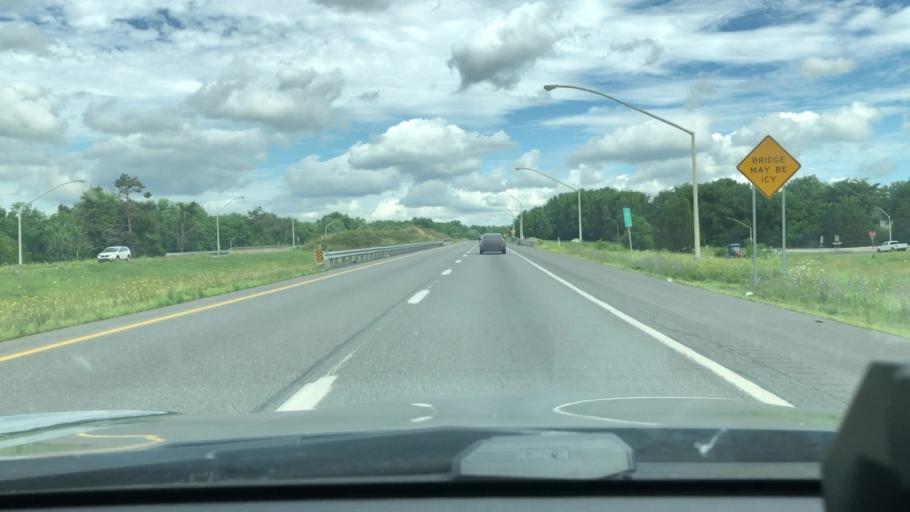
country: US
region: Pennsylvania
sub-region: Northampton County
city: Belfast
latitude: 40.7774
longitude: -75.2817
